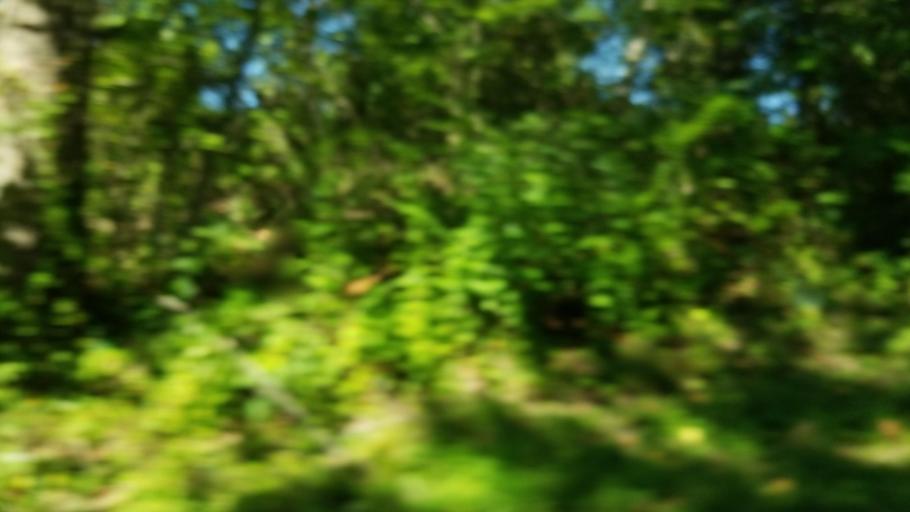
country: US
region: Illinois
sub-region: Williamson County
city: Johnston City
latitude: 37.7849
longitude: -88.8215
